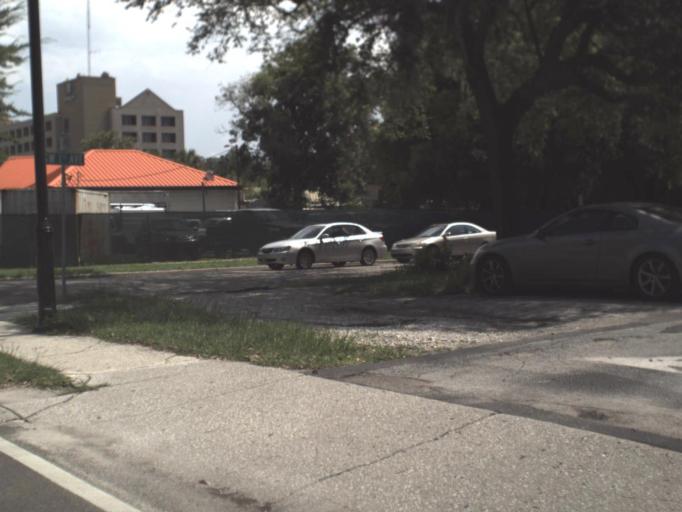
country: US
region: Florida
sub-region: Alachua County
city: Gainesville
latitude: 29.6510
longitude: -82.3393
